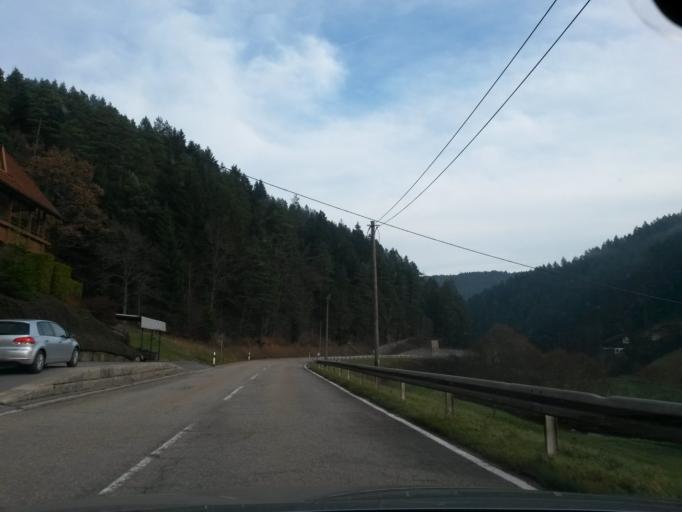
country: DE
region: Baden-Wuerttemberg
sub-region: Freiburg Region
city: Tennenbronn
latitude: 48.1857
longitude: 8.3784
